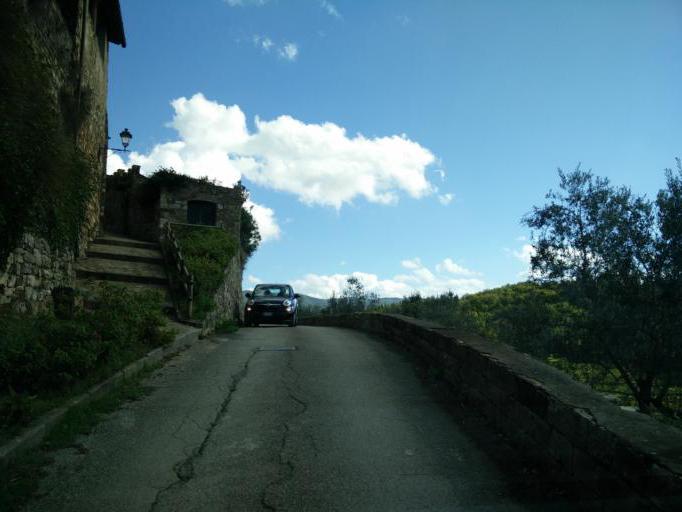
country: IT
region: Tuscany
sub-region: Province of Florence
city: Greve in Chianti
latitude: 43.5803
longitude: 11.3029
